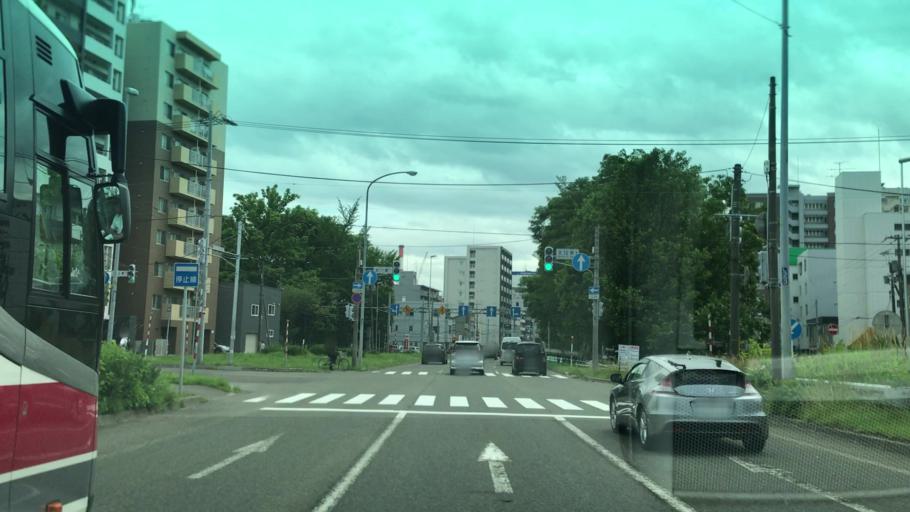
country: JP
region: Hokkaido
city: Sapporo
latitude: 43.0768
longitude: 141.3529
